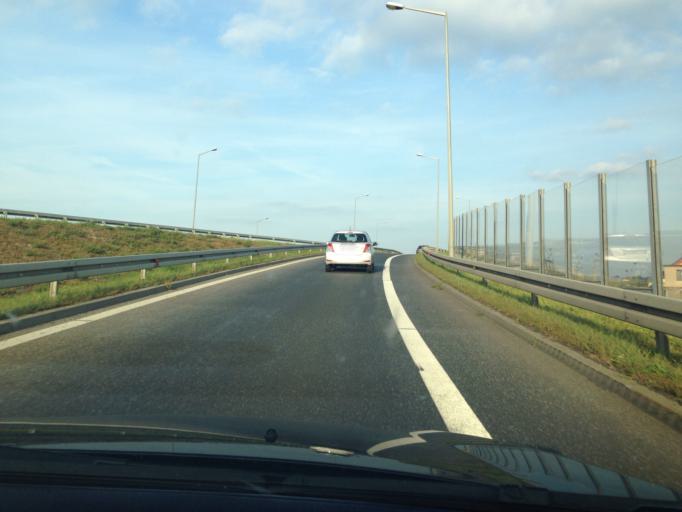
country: PL
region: Greater Poland Voivodeship
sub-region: Powiat gnieznienski
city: Gniezno
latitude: 52.5543
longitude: 17.6225
